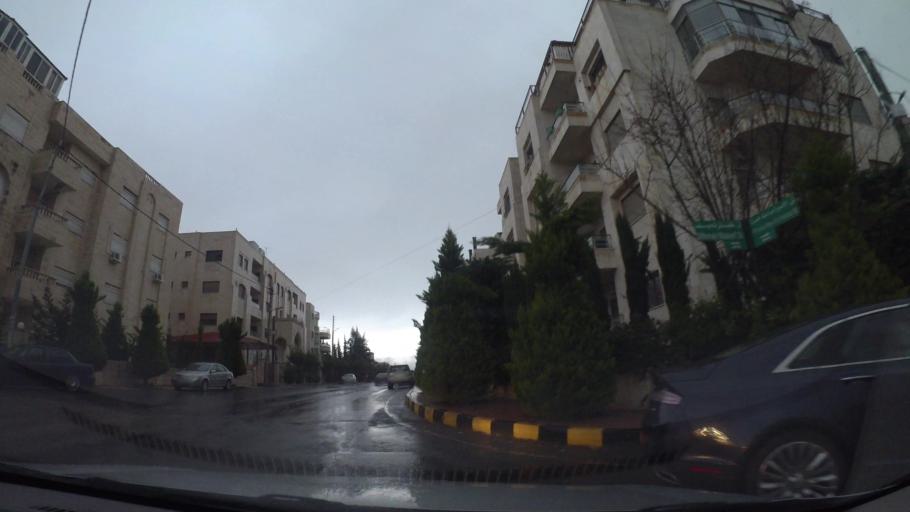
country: JO
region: Amman
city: Umm as Summaq
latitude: 31.9074
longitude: 35.8639
